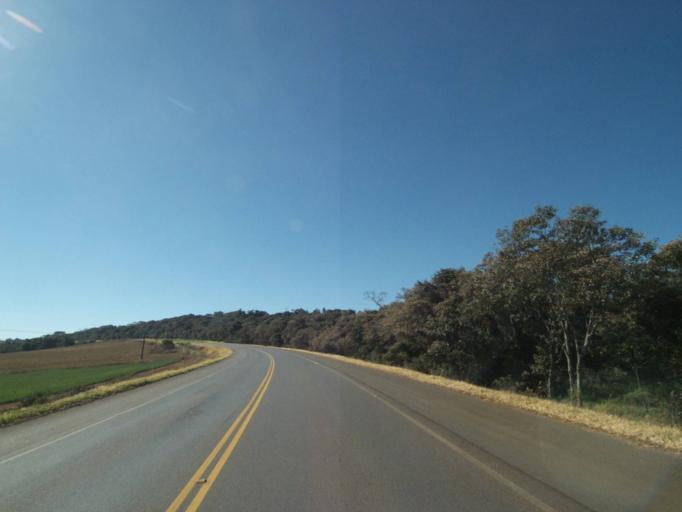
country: BR
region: Parana
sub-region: Tibagi
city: Tibagi
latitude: -24.3788
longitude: -50.3278
